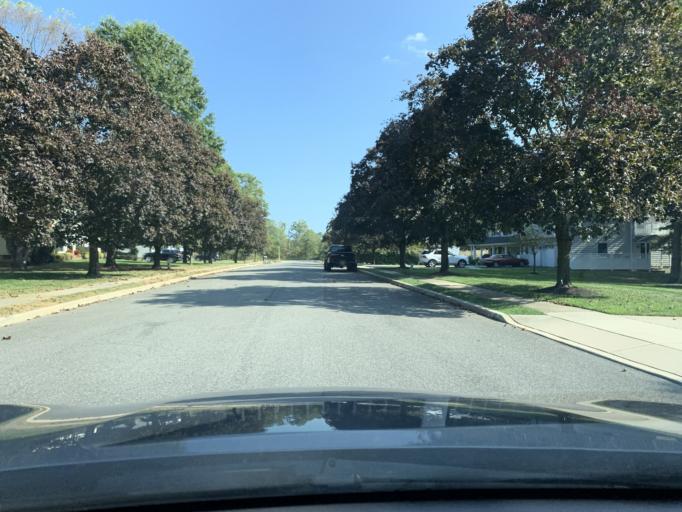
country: US
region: New Jersey
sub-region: Monmouth County
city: Shrewsbury
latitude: 40.3156
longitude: -74.0537
